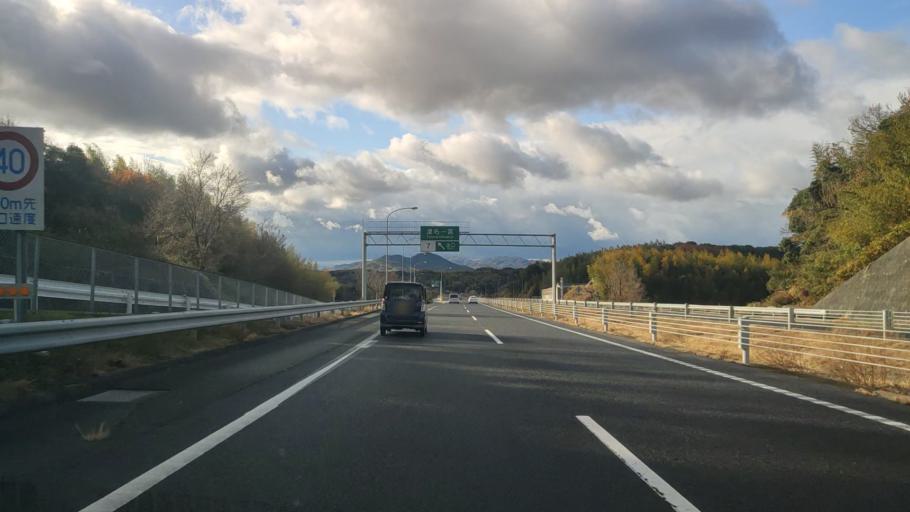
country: JP
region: Hyogo
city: Sumoto
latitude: 34.4475
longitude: 134.8761
